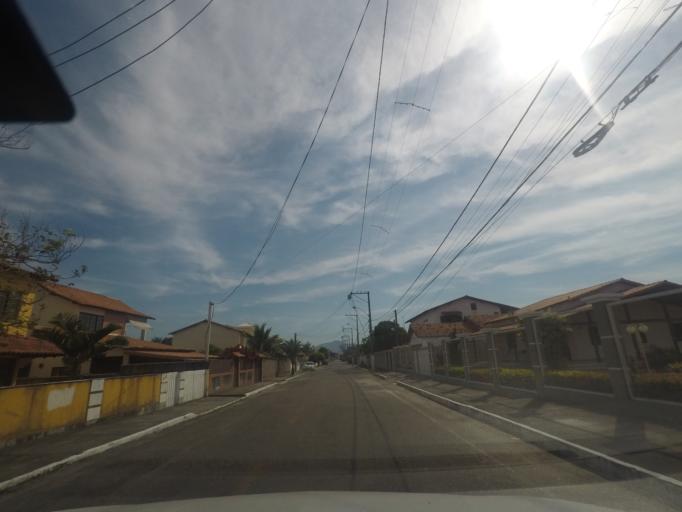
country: BR
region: Rio de Janeiro
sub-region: Marica
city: Marica
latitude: -22.9573
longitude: -42.8128
